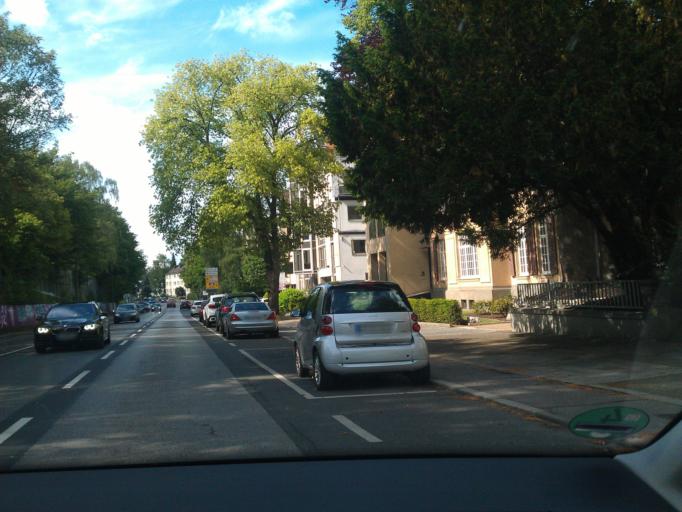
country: DE
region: North Rhine-Westphalia
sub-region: Regierungsbezirk Koln
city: Aachen
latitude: 50.7480
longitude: 6.0872
